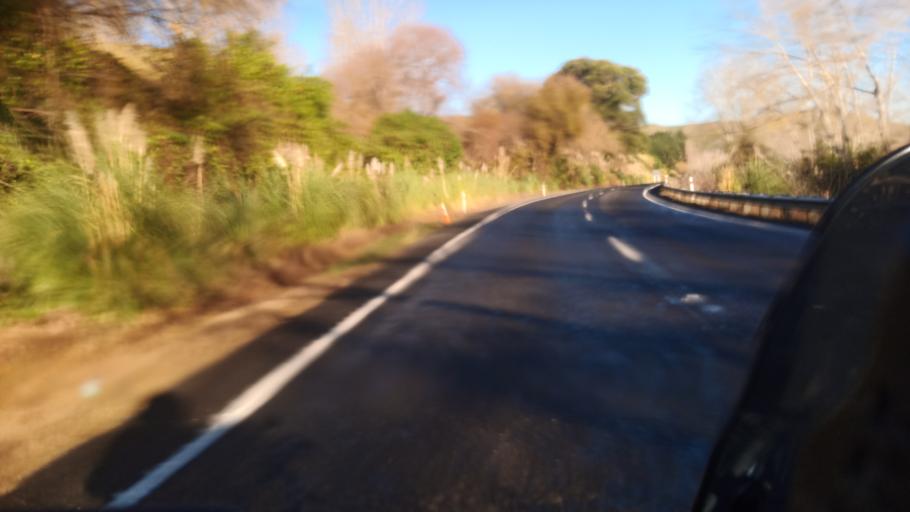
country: NZ
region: Hawke's Bay
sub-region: Wairoa District
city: Wairoa
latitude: -39.0402
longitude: 177.3935
